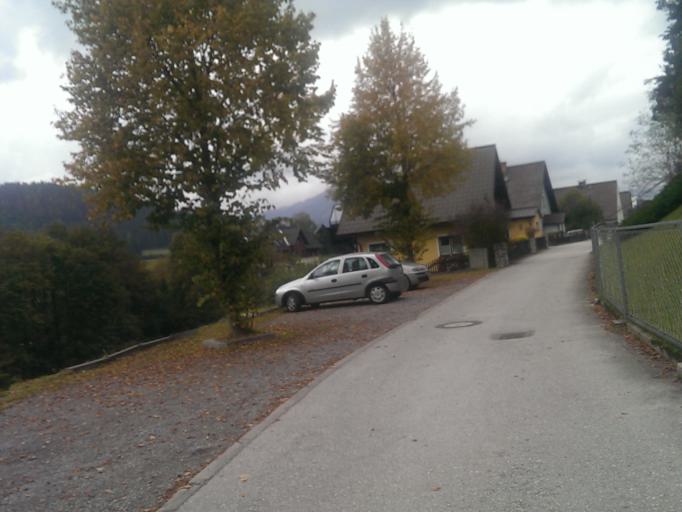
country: AT
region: Styria
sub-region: Politischer Bezirk Bruck-Muerzzuschlag
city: Mariazell
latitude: 47.7796
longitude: 15.3108
